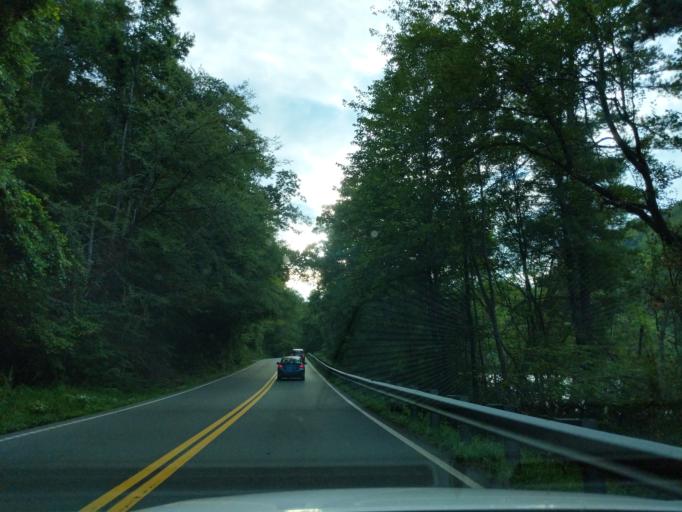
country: US
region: Tennessee
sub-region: Polk County
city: Benton
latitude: 35.1104
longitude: -84.5674
